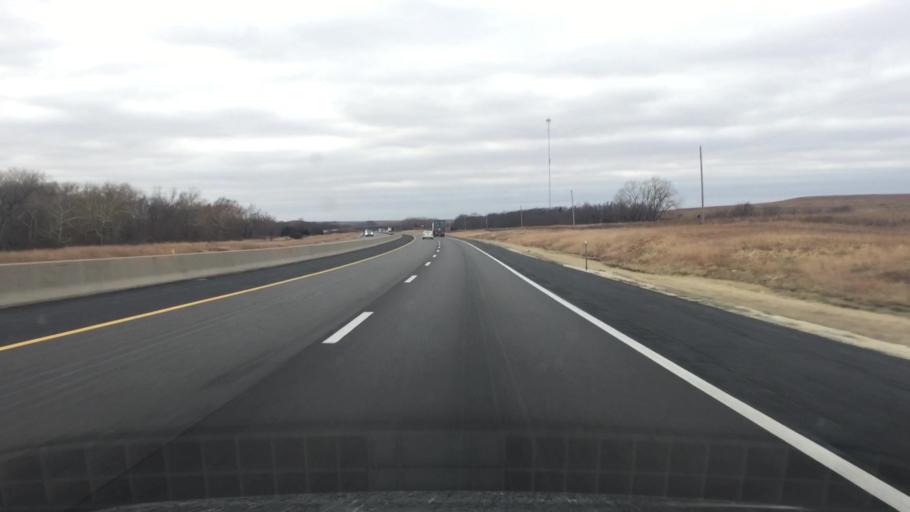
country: US
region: Kansas
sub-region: Chase County
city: Cottonwood Falls
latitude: 38.1486
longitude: -96.5013
